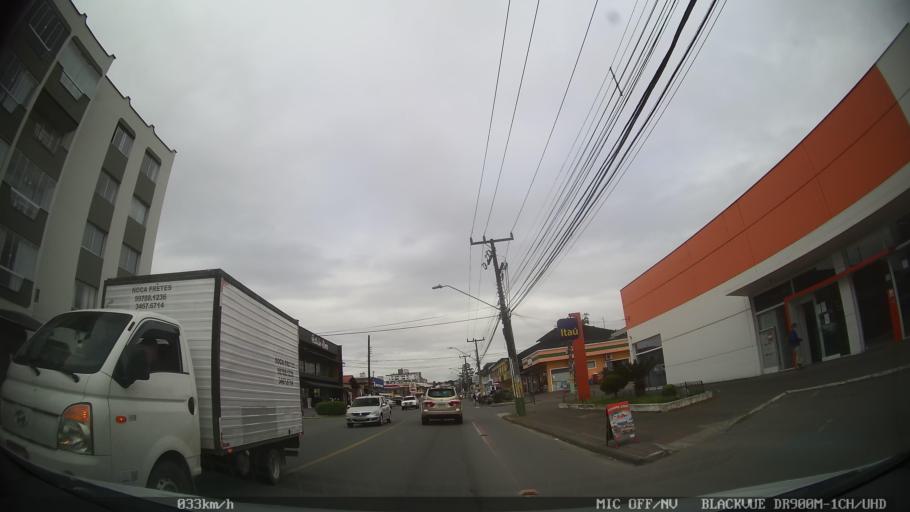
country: BR
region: Santa Catarina
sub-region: Joinville
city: Joinville
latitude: -26.2705
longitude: -48.8722
